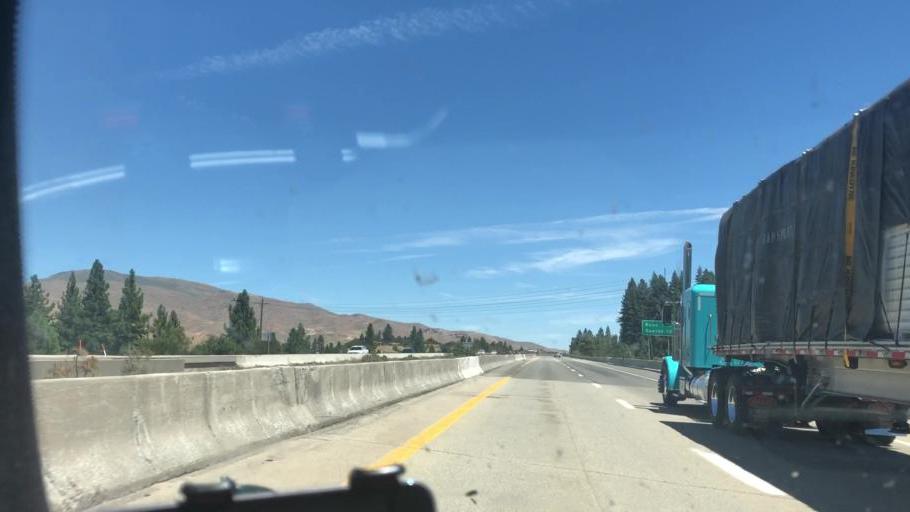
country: US
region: Nevada
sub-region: Washoe County
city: Verdi
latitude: 39.5102
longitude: -119.9952
